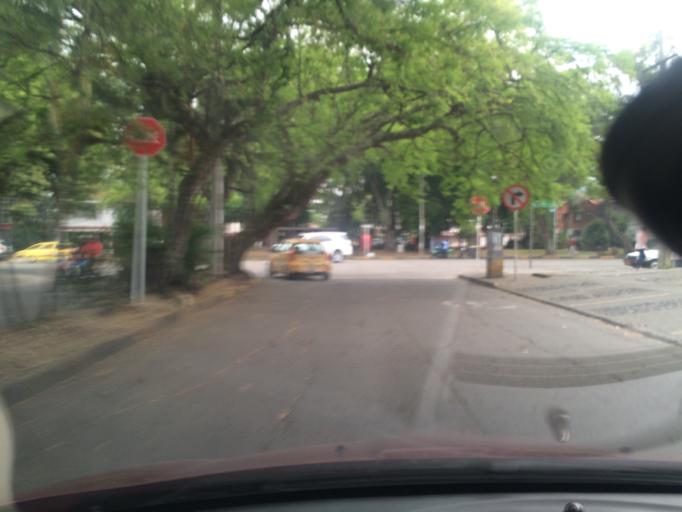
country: CO
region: Valle del Cauca
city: Cali
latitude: 3.4191
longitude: -76.5454
